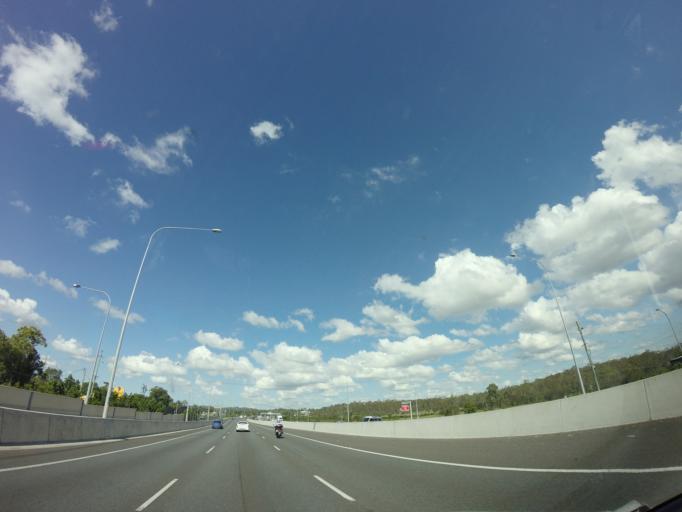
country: AU
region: Queensland
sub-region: Ipswich
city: Redbank
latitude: -27.6031
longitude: 152.8701
